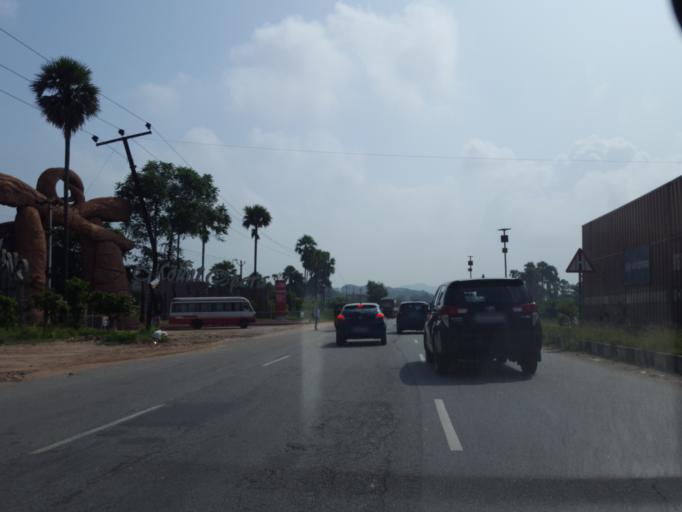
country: IN
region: Telangana
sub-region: Rangareddi
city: Ghatkesar
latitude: 17.3067
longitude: 78.7194
